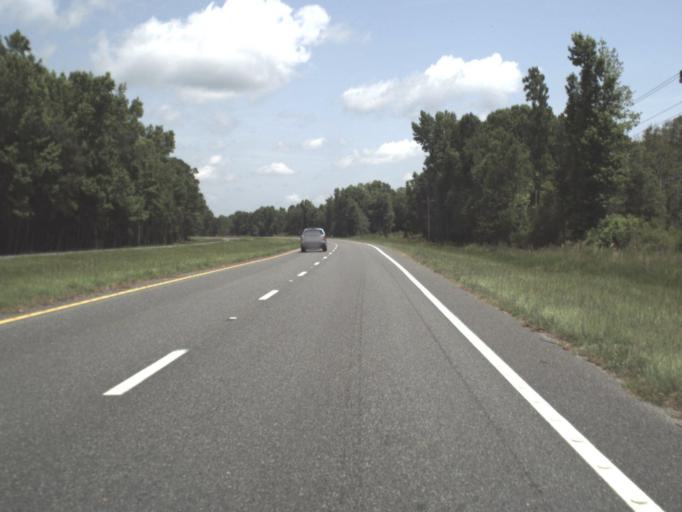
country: US
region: Florida
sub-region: Taylor County
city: Perry
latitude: 29.9426
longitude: -83.4496
